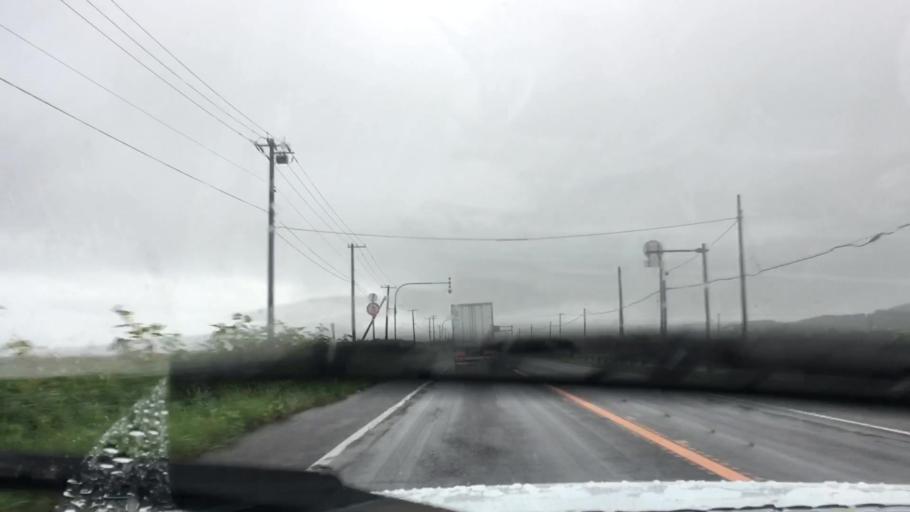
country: JP
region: Hokkaido
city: Niseko Town
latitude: 42.4260
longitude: 140.3158
